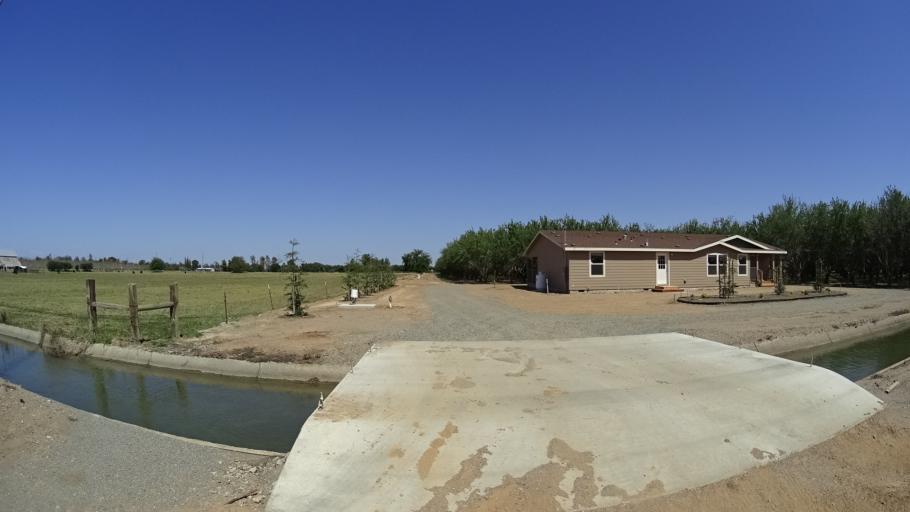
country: US
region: California
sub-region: Glenn County
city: Orland
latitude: 39.7653
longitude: -122.1843
